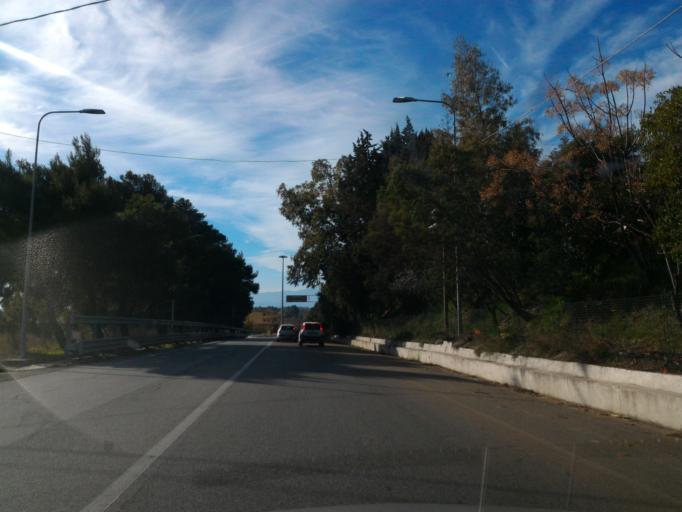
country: IT
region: Calabria
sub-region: Provincia di Catanzaro
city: Sellia Marina
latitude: 38.8865
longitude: 16.7139
